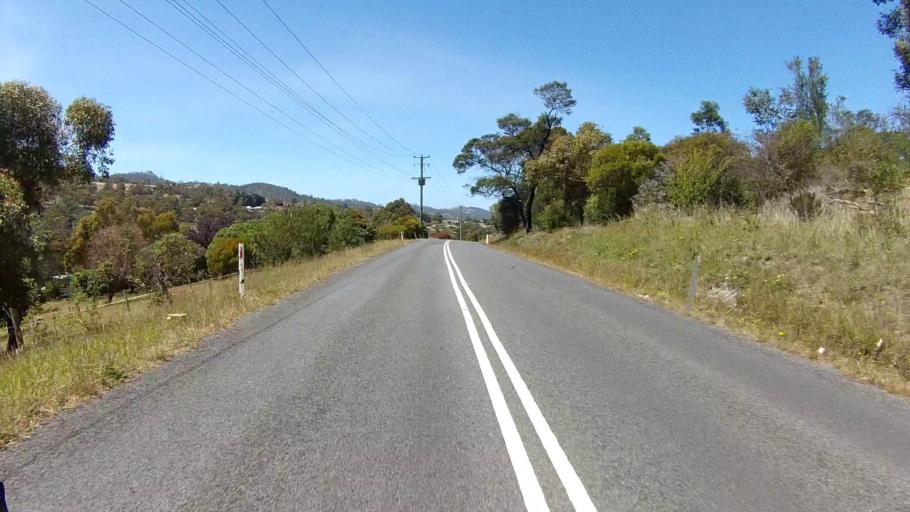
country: AU
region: Tasmania
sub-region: Clarence
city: Howrah
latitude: -42.8631
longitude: 147.4181
